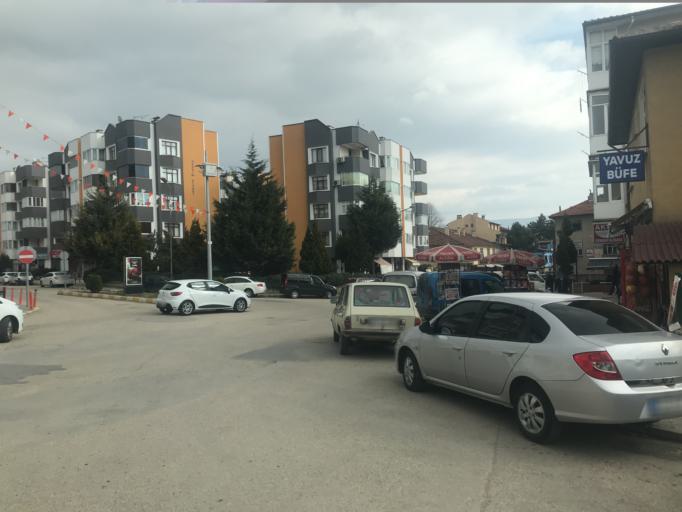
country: TR
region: Karabuk
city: Safranbolu
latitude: 41.2517
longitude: 32.6830
